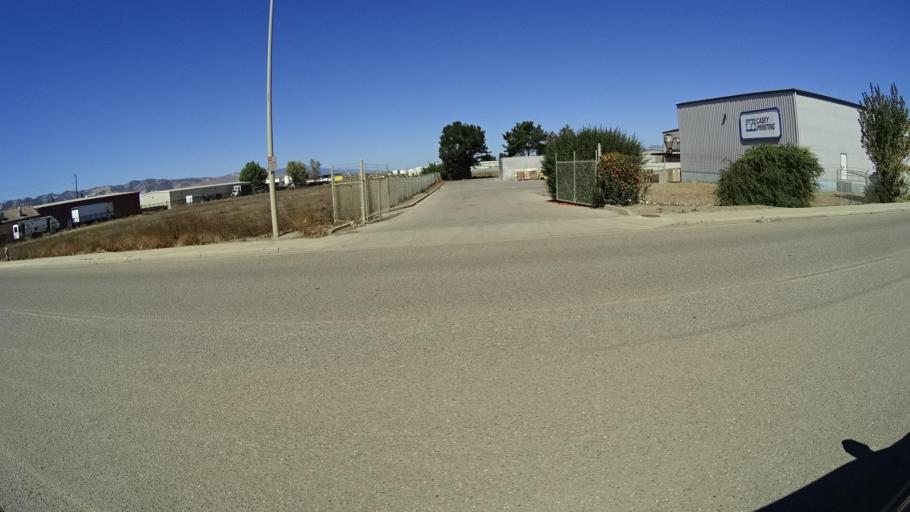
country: US
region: California
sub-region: Monterey County
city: King City
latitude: 36.2194
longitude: -121.1212
